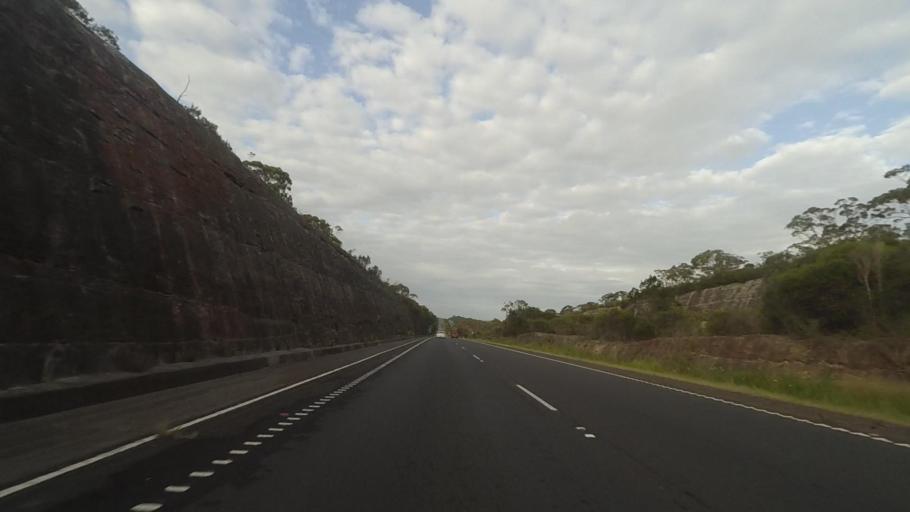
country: AU
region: New South Wales
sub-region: Wollongong
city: Helensburgh
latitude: -34.2203
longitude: 150.9534
